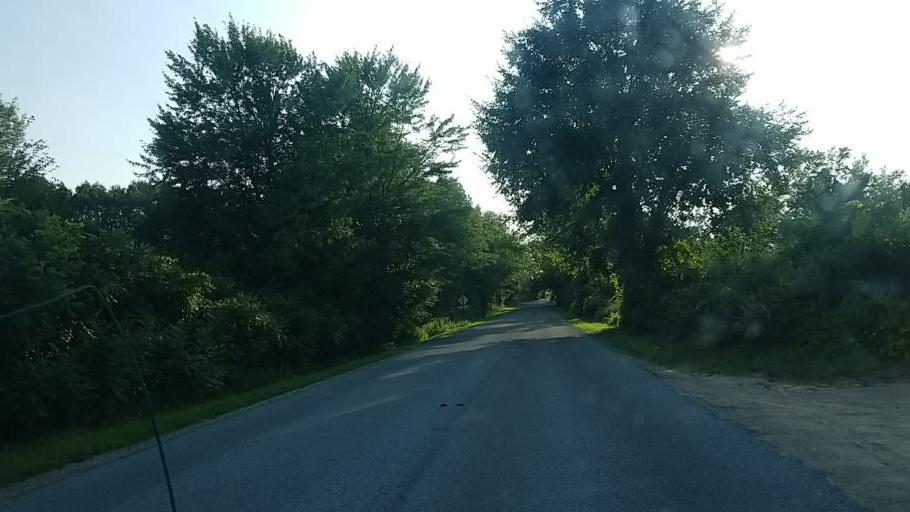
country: US
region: Michigan
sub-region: Montcalm County
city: Greenville
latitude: 43.2338
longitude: -85.3540
